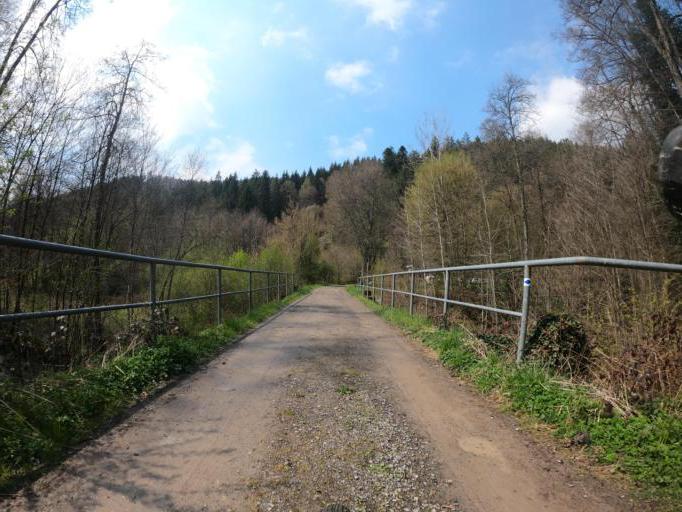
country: DE
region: Baden-Wuerttemberg
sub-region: Karlsruhe Region
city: Bad Wildbad
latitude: 48.7275
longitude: 8.5700
